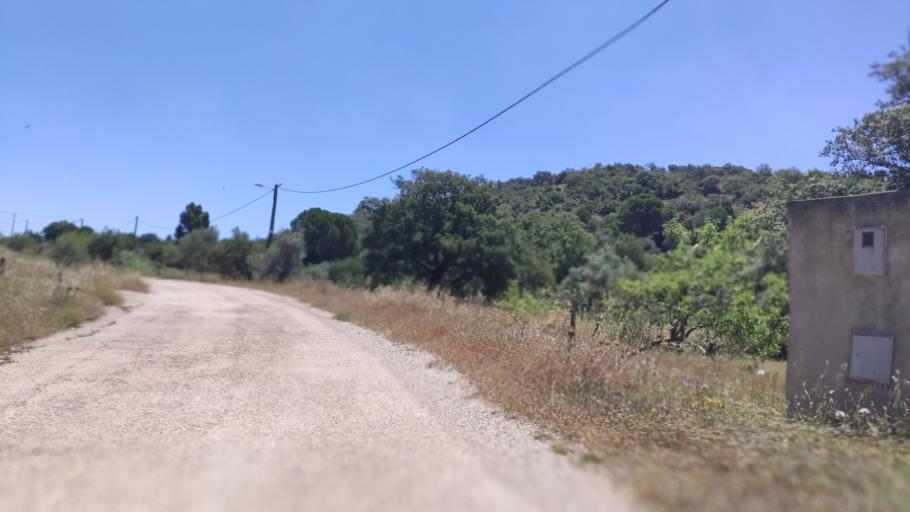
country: PT
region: Faro
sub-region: Sao Bras de Alportel
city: Sao Bras de Alportel
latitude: 37.1736
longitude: -7.9235
